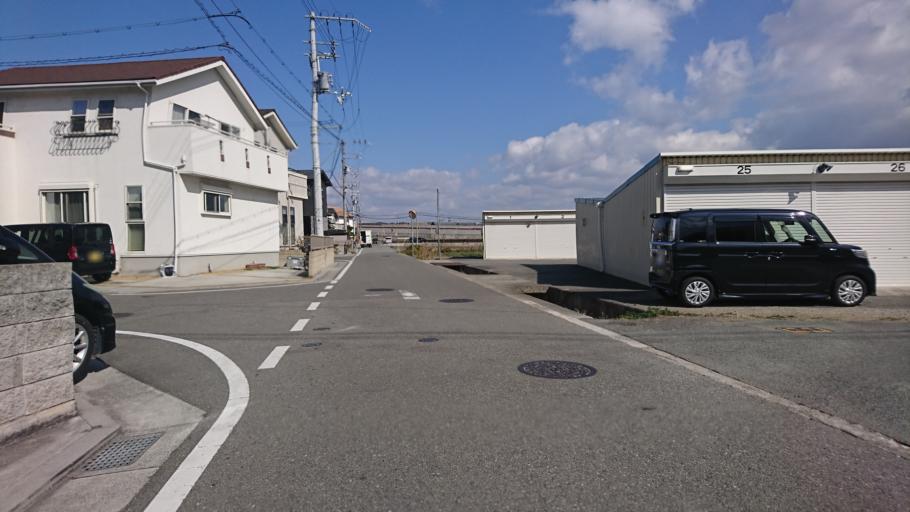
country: JP
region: Hyogo
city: Kakogawacho-honmachi
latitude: 34.7891
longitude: 134.8076
